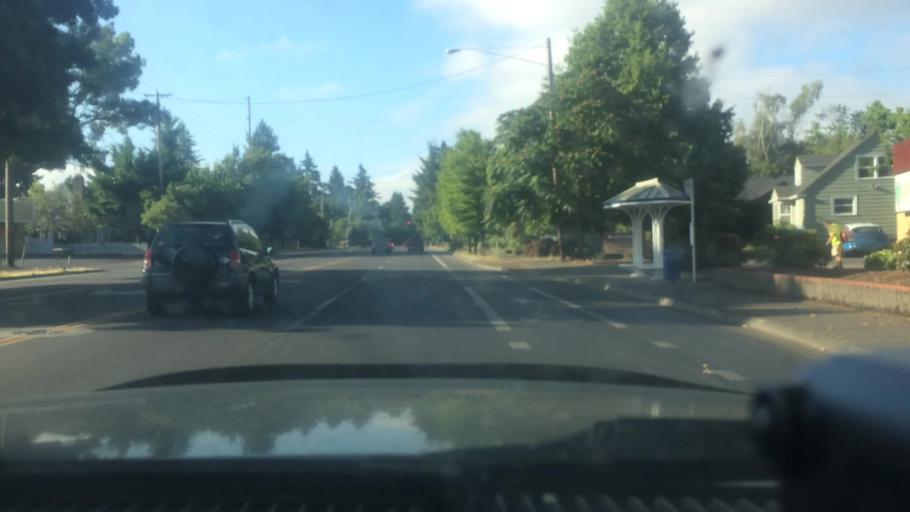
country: US
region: Oregon
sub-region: Lane County
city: Eugene
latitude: 44.0766
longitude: -123.1202
